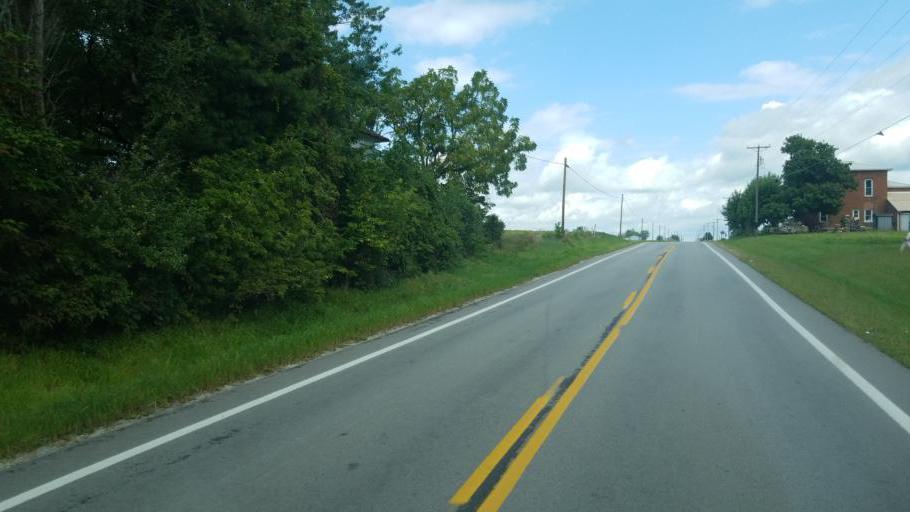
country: US
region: Ohio
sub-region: Seneca County
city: Tiffin
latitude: 41.0735
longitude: -83.0153
